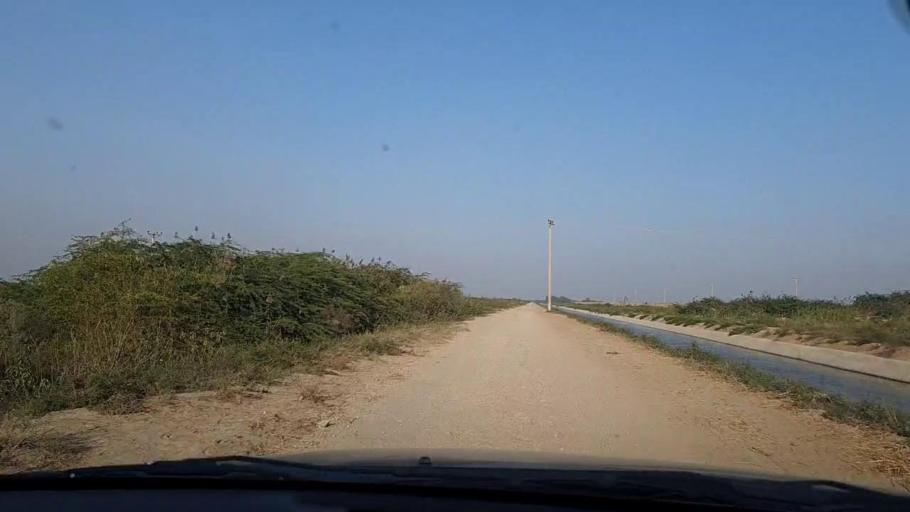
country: PK
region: Sindh
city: Chuhar Jamali
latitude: 24.2809
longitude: 67.7426
